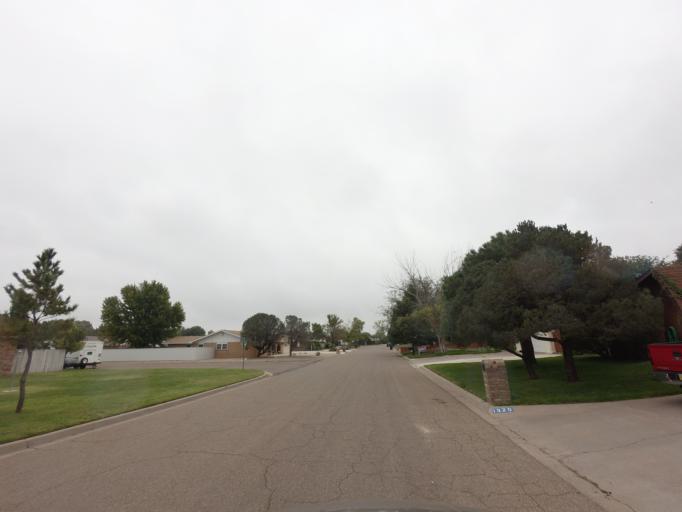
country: US
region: New Mexico
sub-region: Curry County
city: Clovis
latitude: 34.4399
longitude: -103.1809
